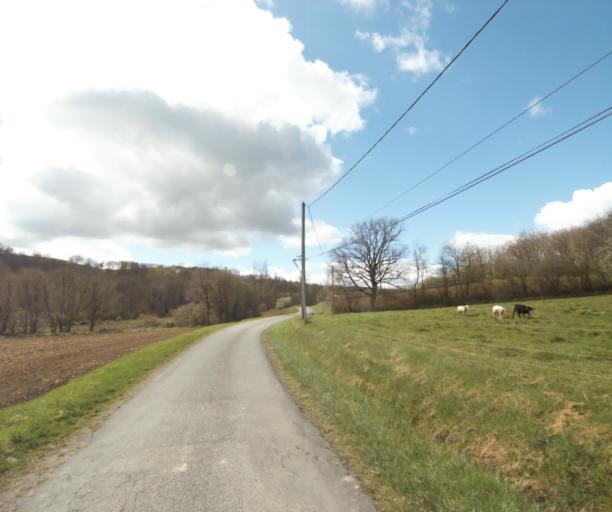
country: FR
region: Midi-Pyrenees
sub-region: Departement de l'Ariege
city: Saverdun
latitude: 43.1954
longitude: 1.5669
